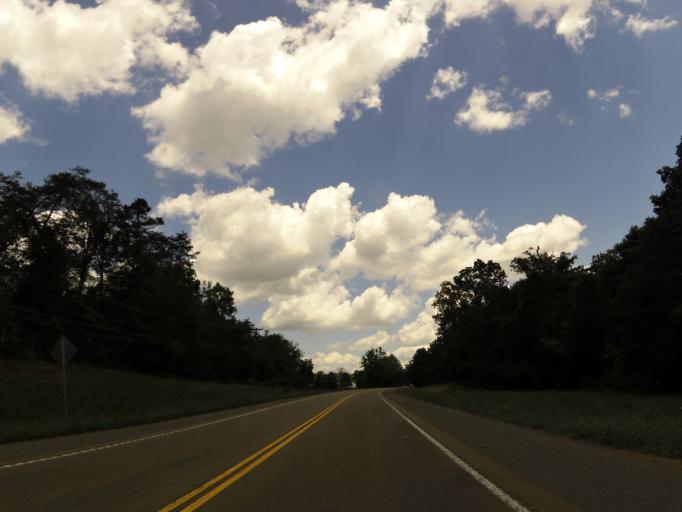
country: US
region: Tennessee
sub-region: Union County
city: Condon
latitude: 36.2071
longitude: -83.8738
